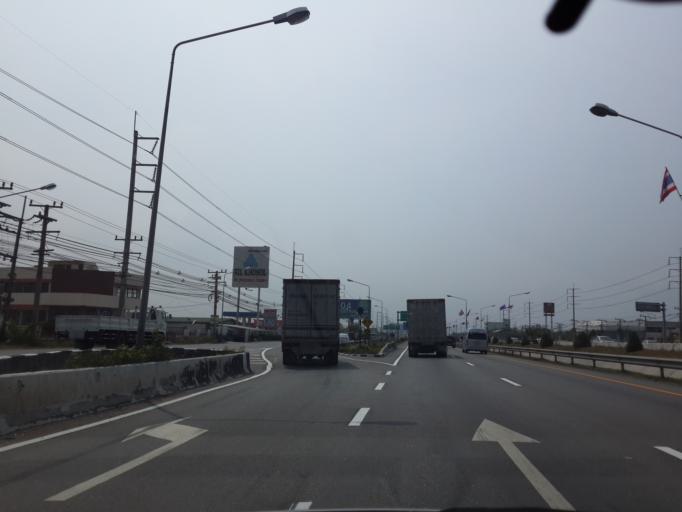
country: TH
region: Chon Buri
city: Chon Buri
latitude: 13.4419
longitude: 101.0004
